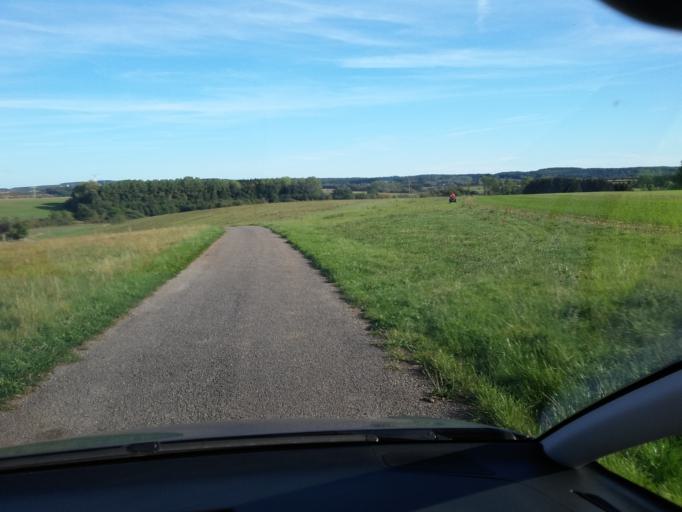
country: BE
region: Wallonia
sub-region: Province du Luxembourg
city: Habay-la-Vieille
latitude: 49.7086
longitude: 5.7009
